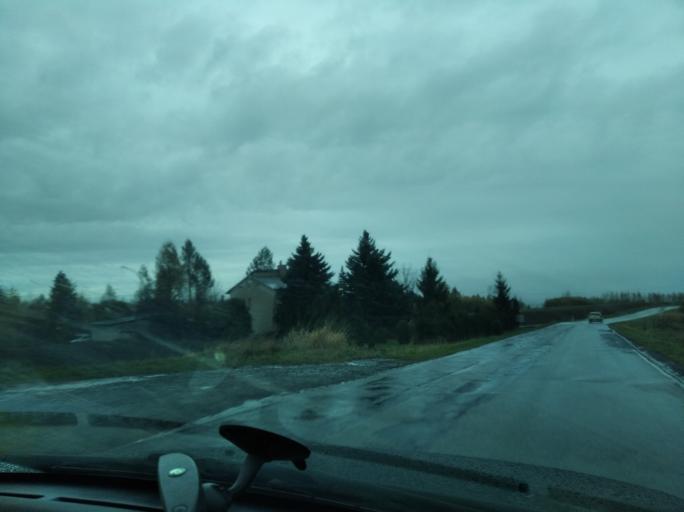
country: PL
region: Subcarpathian Voivodeship
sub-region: Powiat lancucki
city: Handzlowka
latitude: 49.9995
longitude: 22.1988
